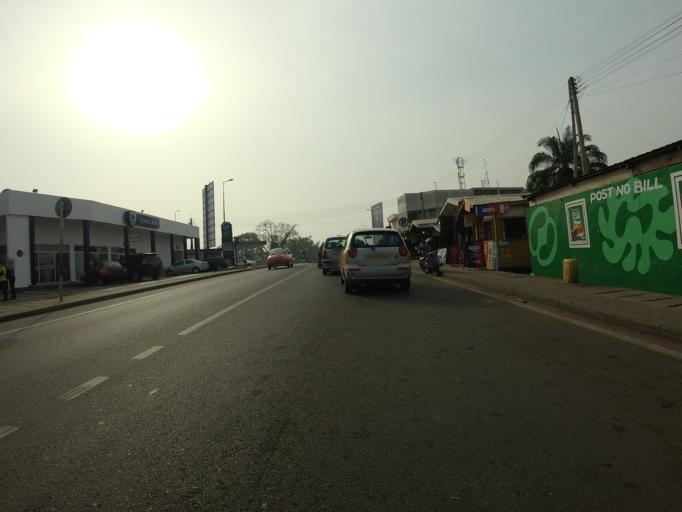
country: GH
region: Volta
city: Ho
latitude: 6.6076
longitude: 0.4724
